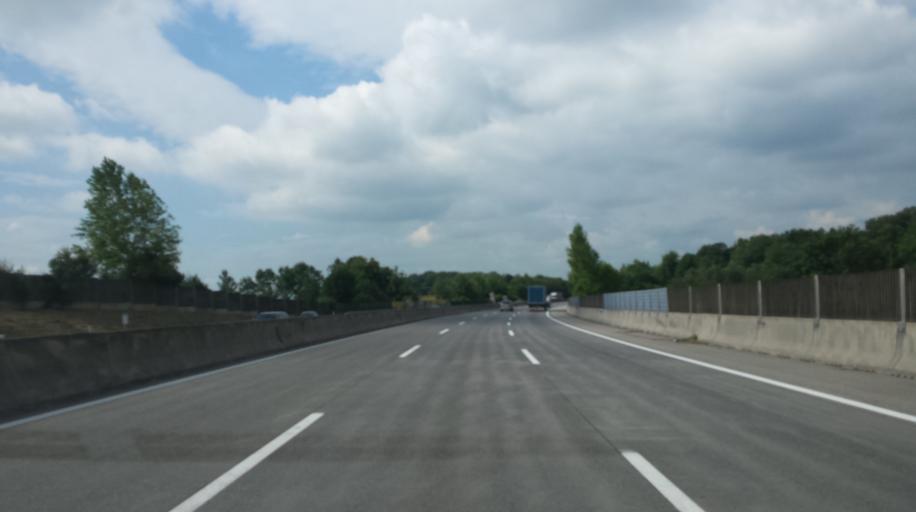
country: AT
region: Lower Austria
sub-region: Politischer Bezirk Amstetten
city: Zeillern
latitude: 48.1276
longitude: 14.8245
